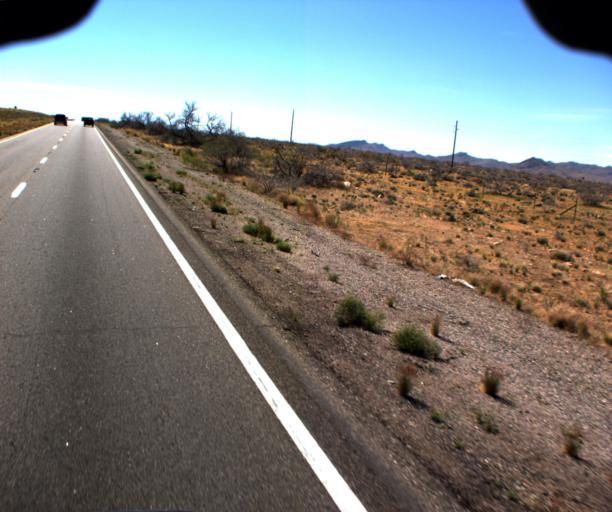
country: US
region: Arizona
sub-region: Mohave County
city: Dolan Springs
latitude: 35.4483
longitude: -114.2964
